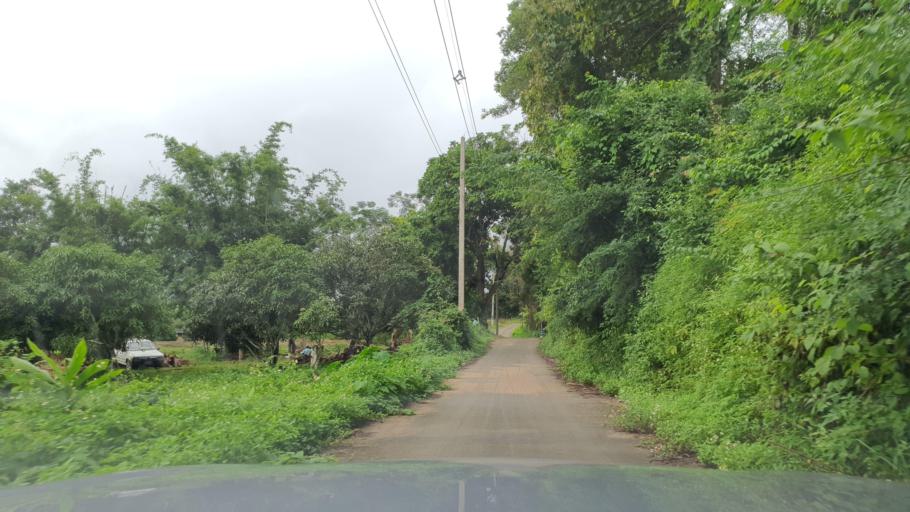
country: TH
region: Chiang Mai
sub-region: Amphoe Chiang Dao
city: Chiang Dao
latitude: 19.3358
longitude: 98.9277
